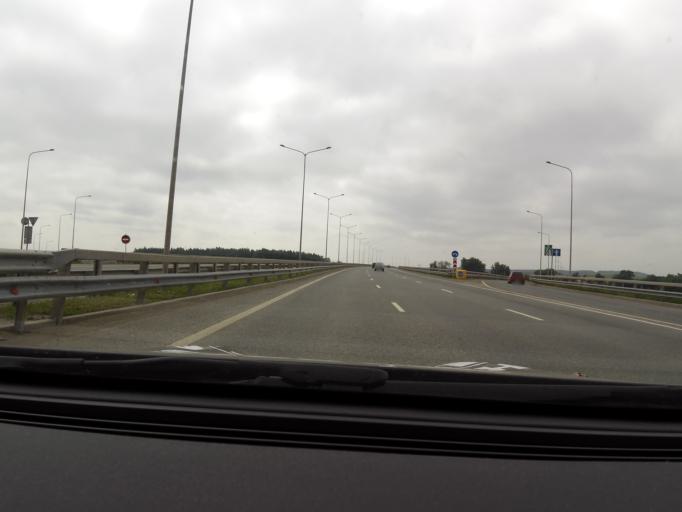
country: RU
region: Perm
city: Froly
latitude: 57.8829
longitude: 56.2668
